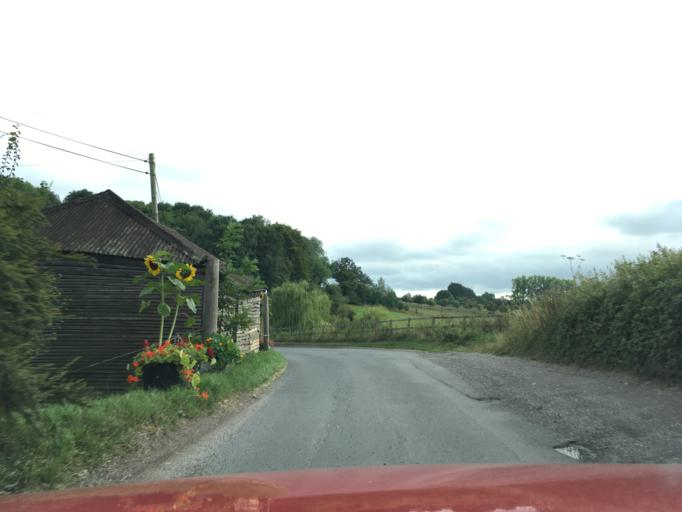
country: GB
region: England
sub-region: Hampshire
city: Colden Common
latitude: 51.0002
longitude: -1.2722
